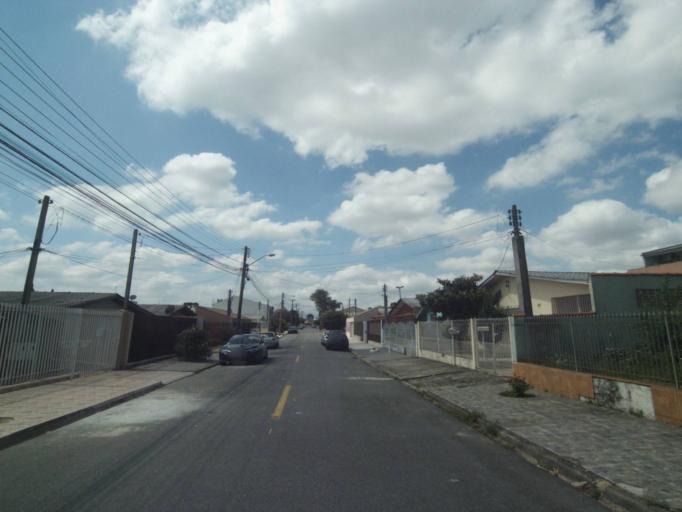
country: BR
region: Parana
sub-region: Curitiba
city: Curitiba
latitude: -25.5143
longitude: -49.3222
